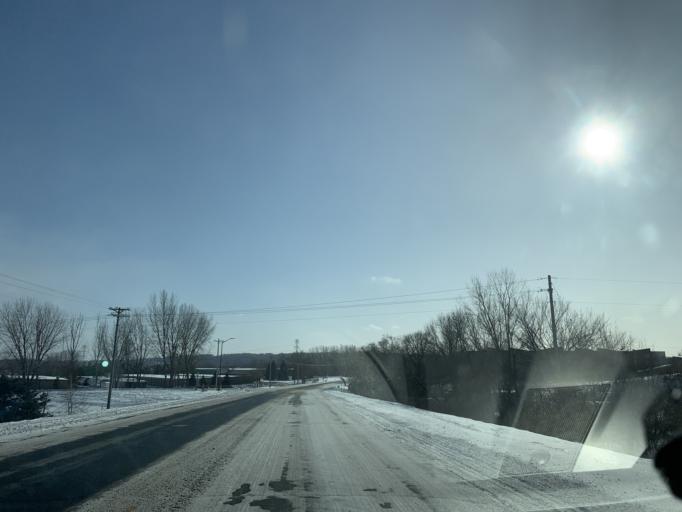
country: US
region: Minnesota
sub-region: Scott County
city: Prior Lake
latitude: 44.7833
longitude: -93.4081
